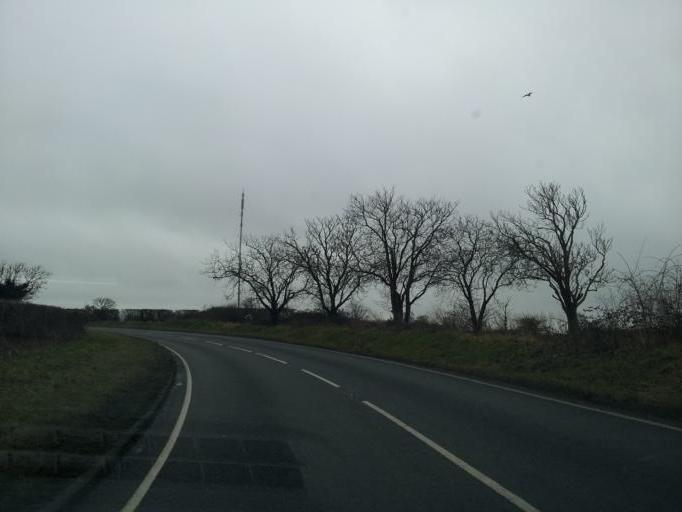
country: GB
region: England
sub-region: Essex
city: Mistley
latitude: 51.9284
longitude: 1.0796
